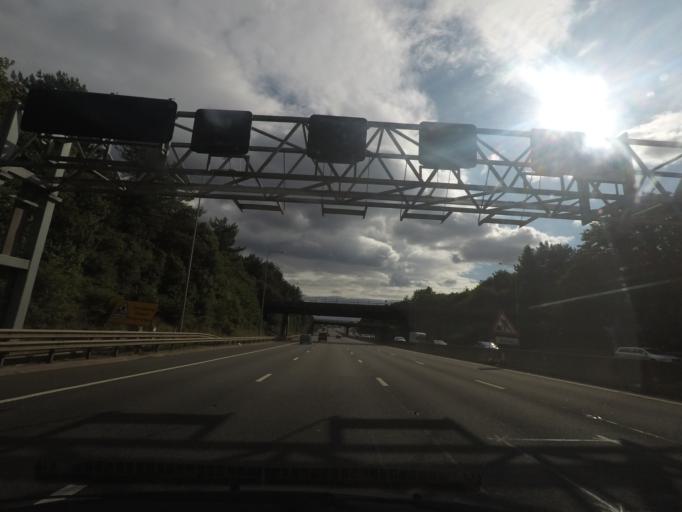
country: GB
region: England
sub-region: Nottinghamshire
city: Kimberley
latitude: 52.9502
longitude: -1.2772
